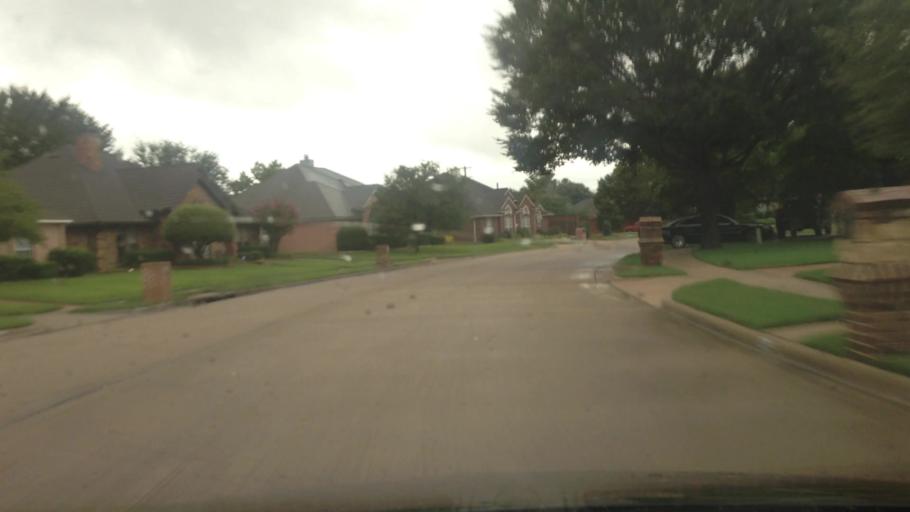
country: US
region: Texas
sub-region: Tarrant County
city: Colleyville
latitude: 32.8795
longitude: -97.1799
